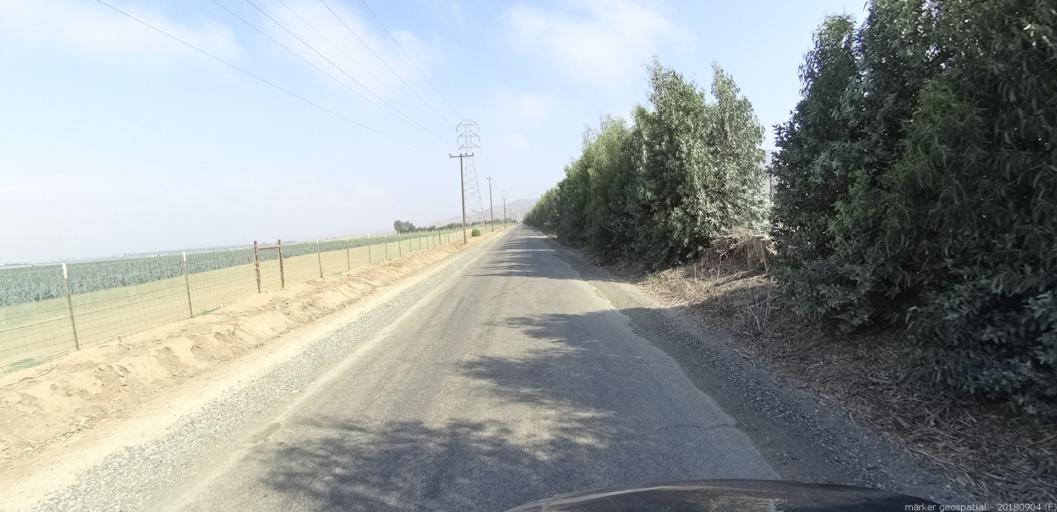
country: US
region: California
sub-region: Monterey County
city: Soledad
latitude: 36.4487
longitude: -121.3318
